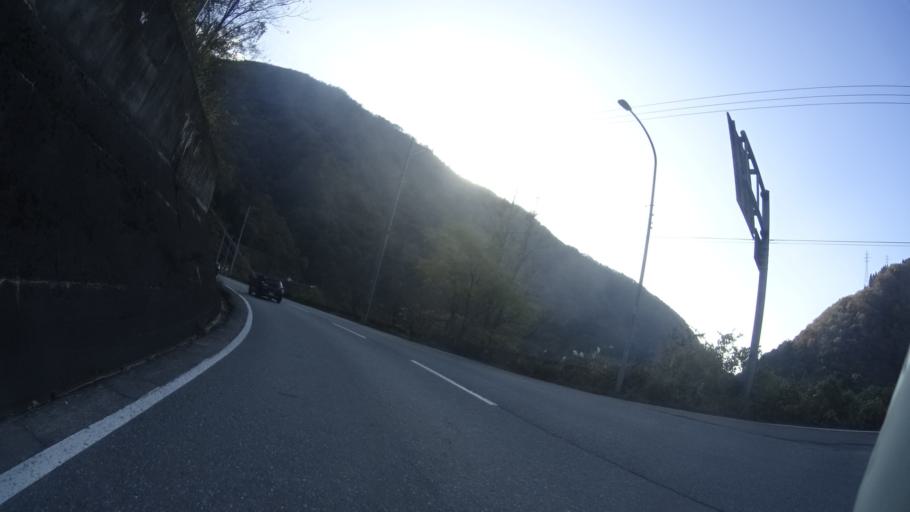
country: JP
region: Fukui
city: Ono
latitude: 35.9678
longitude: 136.5930
